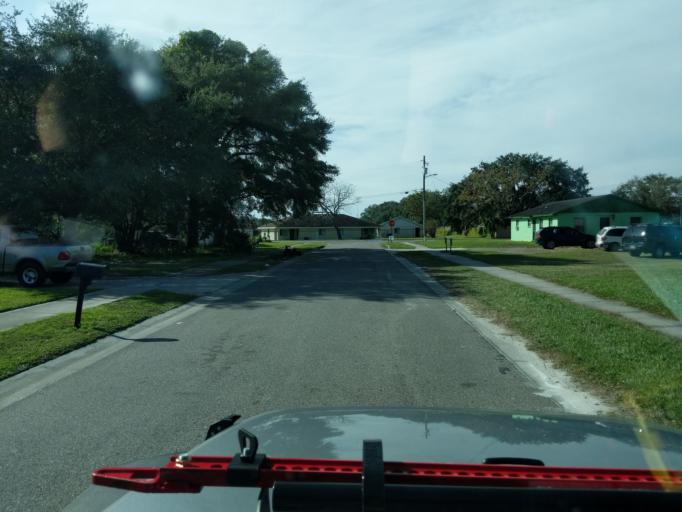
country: US
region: Florida
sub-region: Orange County
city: Winter Garden
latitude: 28.5669
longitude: -81.5662
